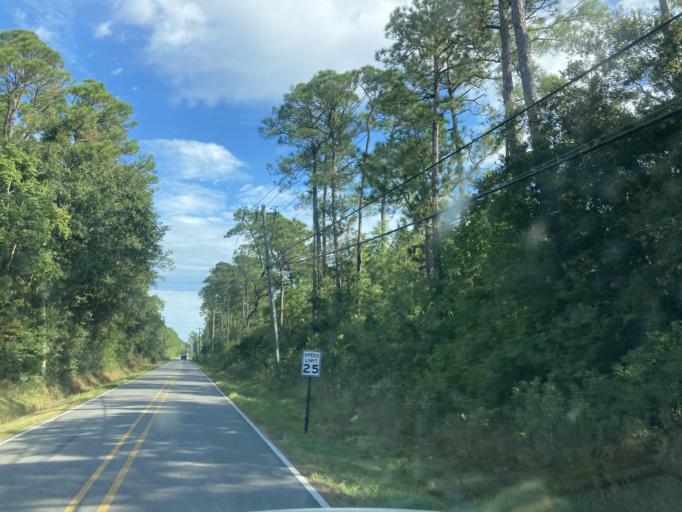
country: US
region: Mississippi
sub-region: Jackson County
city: Saint Martin
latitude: 30.4361
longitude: -88.8665
